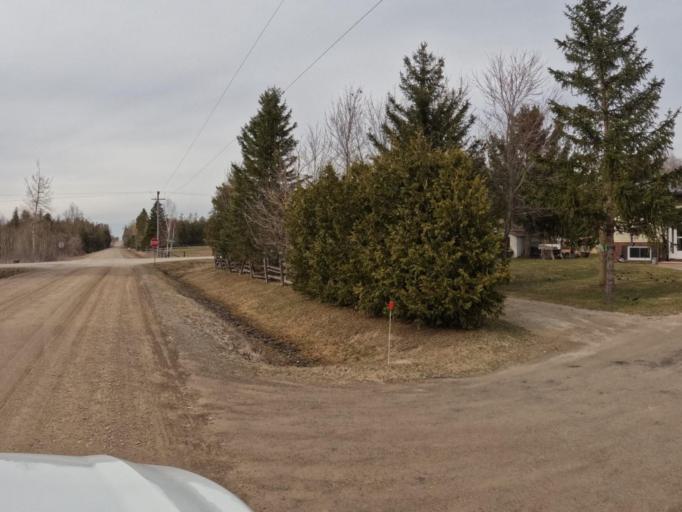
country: CA
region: Ontario
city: Shelburne
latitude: 43.9424
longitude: -80.2604
